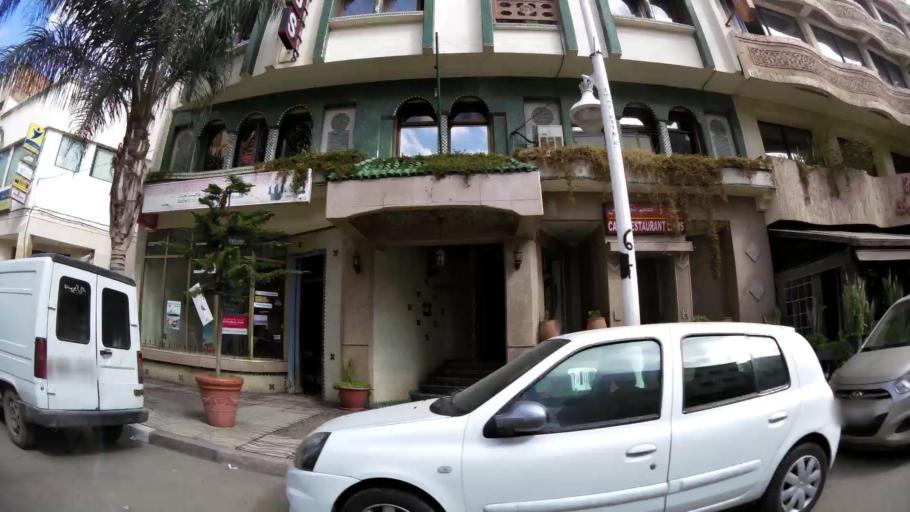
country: MA
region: Oriental
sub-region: Nador
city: Nador
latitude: 35.1722
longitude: -2.9273
